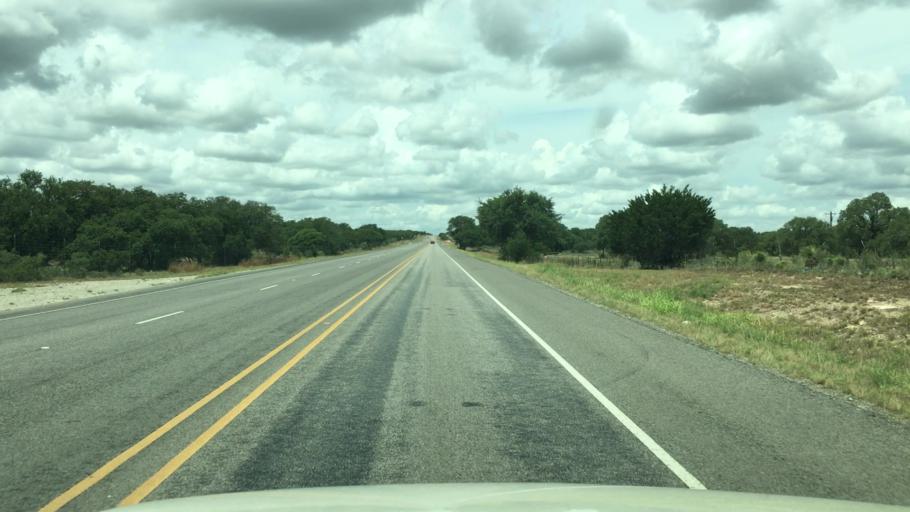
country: US
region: Texas
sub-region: McCulloch County
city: Brady
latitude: 31.0249
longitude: -99.2213
